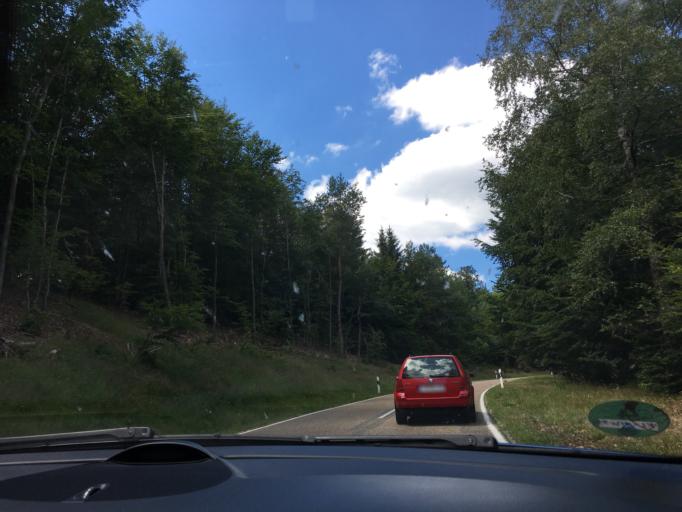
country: DE
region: Rheinland-Pfalz
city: Hauenstein
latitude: 49.2327
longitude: 7.8398
